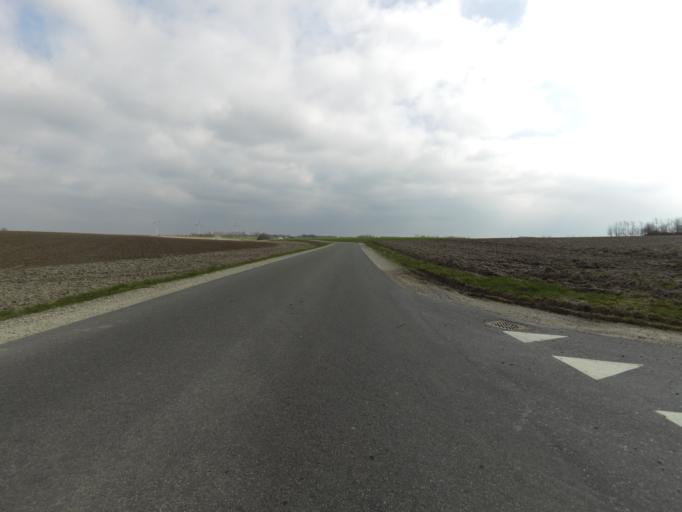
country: DK
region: Central Jutland
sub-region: Holstebro Kommune
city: Holstebro
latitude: 56.4356
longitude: 8.6712
